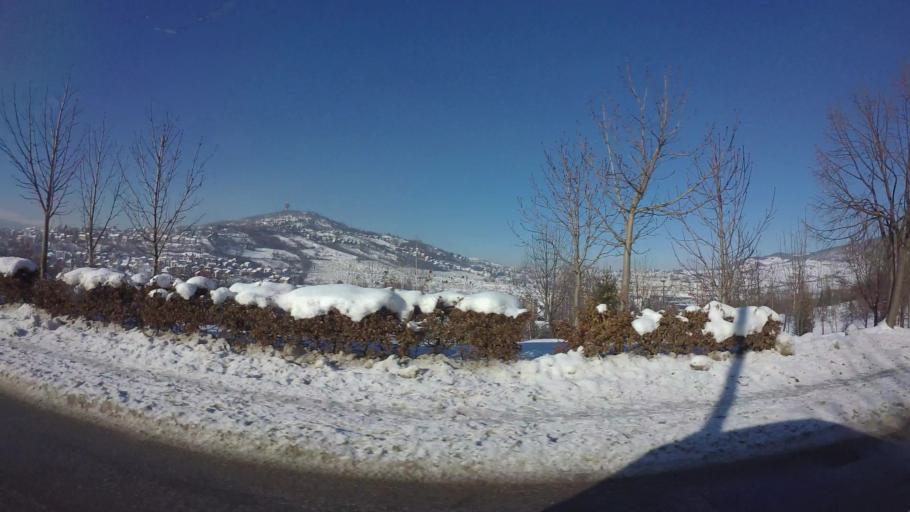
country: BA
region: Federation of Bosnia and Herzegovina
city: Kobilja Glava
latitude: 43.8745
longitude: 18.4074
